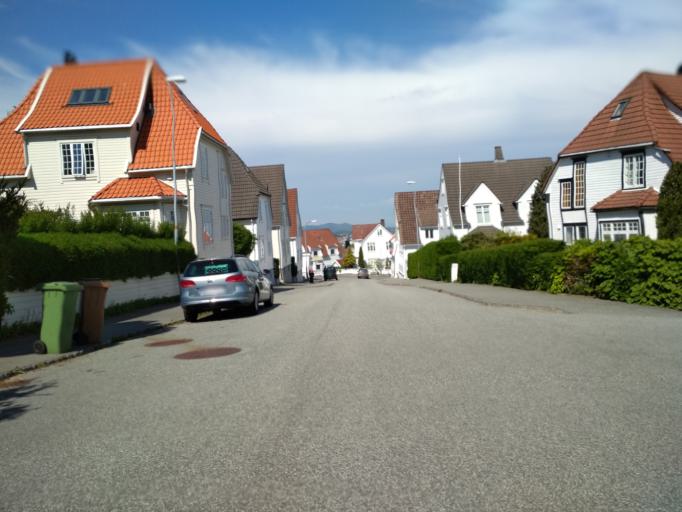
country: NO
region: Rogaland
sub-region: Stavanger
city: Stavanger
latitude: 58.9580
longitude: 5.7337
